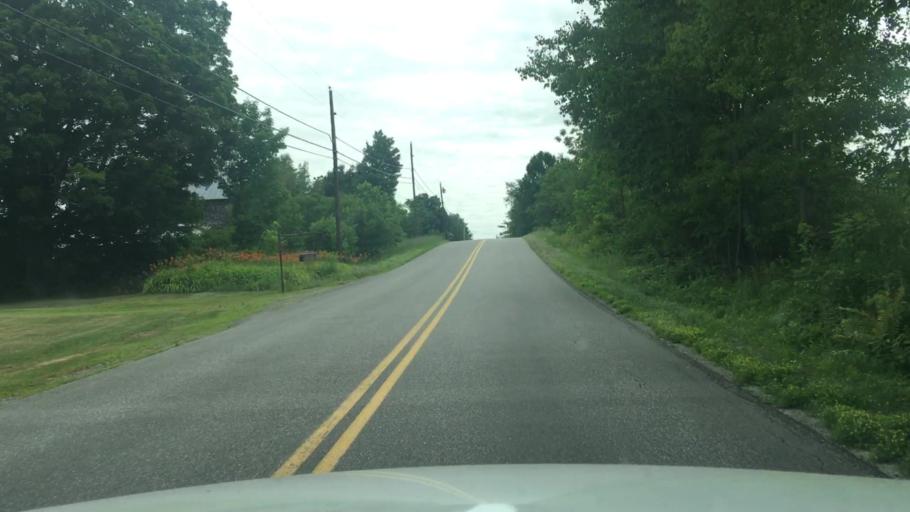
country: US
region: Maine
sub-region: Kennebec County
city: Benton
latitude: 44.5815
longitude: -69.5015
